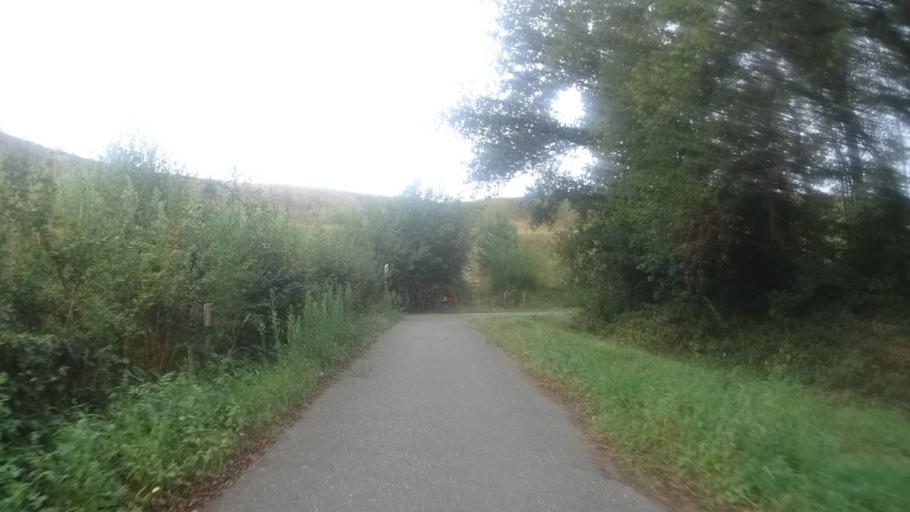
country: NL
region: Limburg
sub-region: Gemeente Venlo
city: Arcen
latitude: 51.4413
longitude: 6.1657
